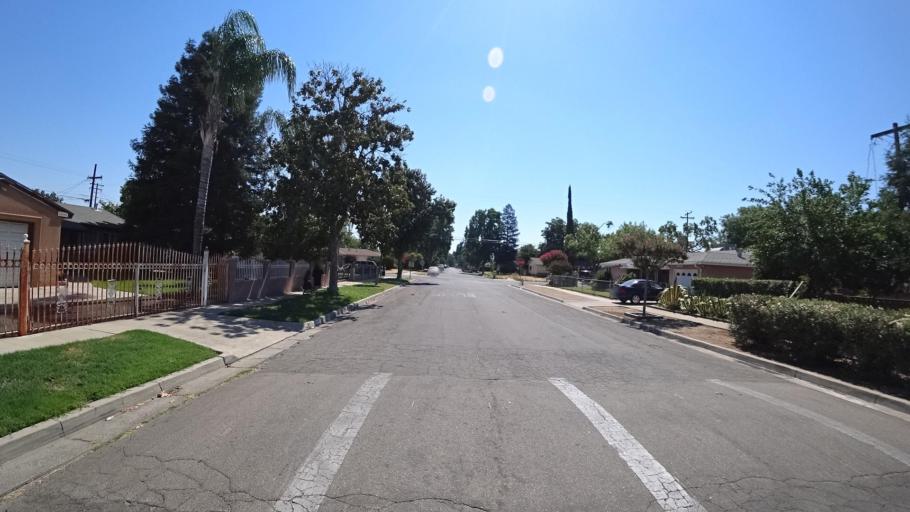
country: US
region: California
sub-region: Fresno County
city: Fresno
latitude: 36.7998
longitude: -119.7774
